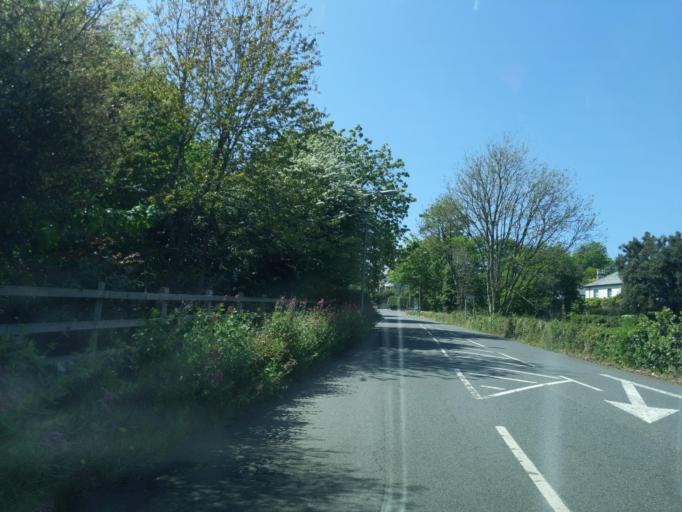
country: GB
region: England
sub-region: Cornwall
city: Pillaton
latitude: 50.3937
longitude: -4.3083
